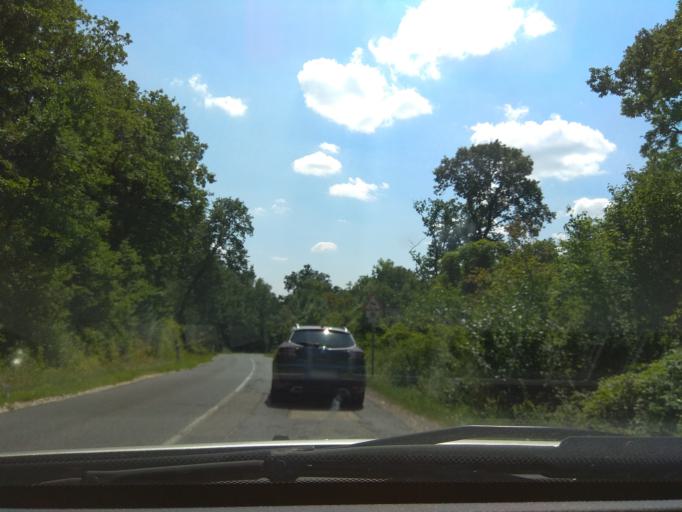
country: HU
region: Borsod-Abauj-Zemplen
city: Harsany
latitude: 48.0205
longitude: 20.7631
